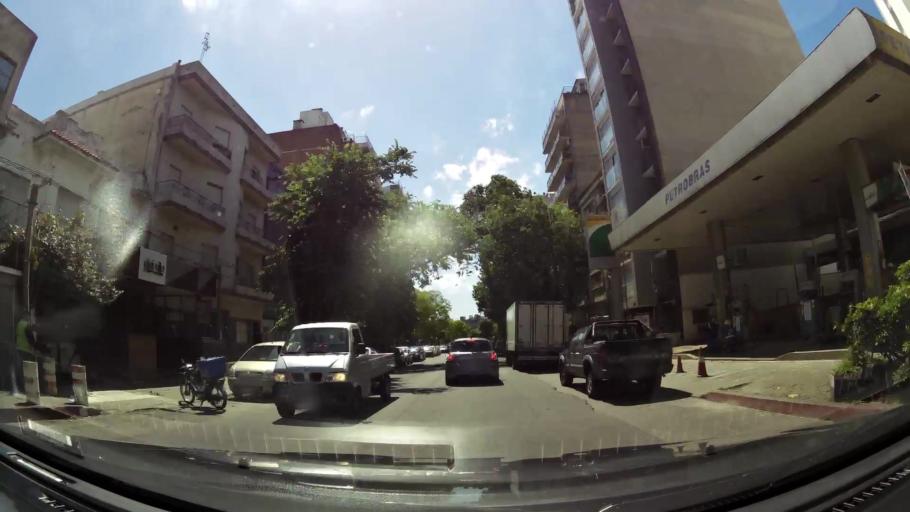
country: UY
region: Montevideo
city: Montevideo
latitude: -34.9138
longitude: -56.1616
